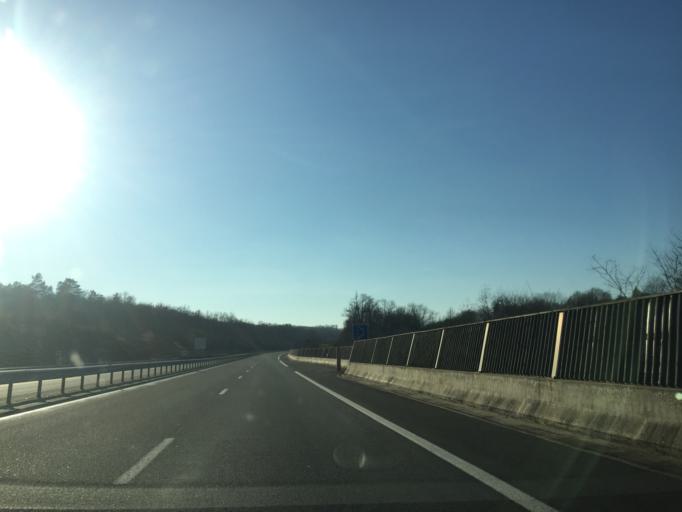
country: FR
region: Limousin
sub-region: Departement de la Correze
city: Mansac
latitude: 45.1595
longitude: 1.3955
